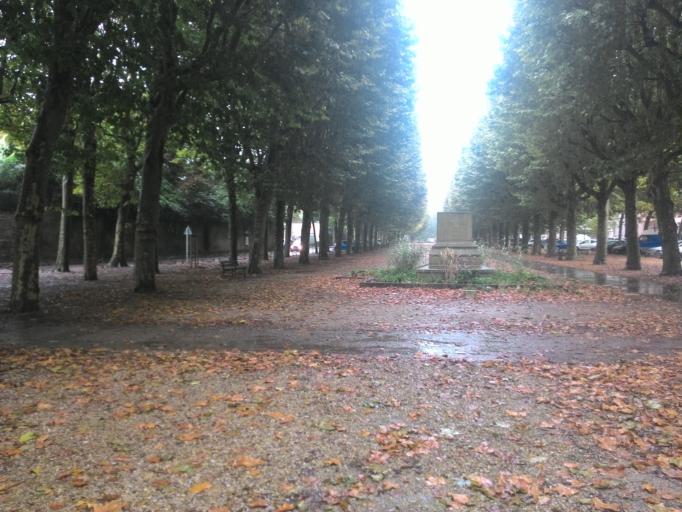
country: FR
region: Bourgogne
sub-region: Departement de l'Yonne
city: Sens
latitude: 48.1951
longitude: 3.2768
